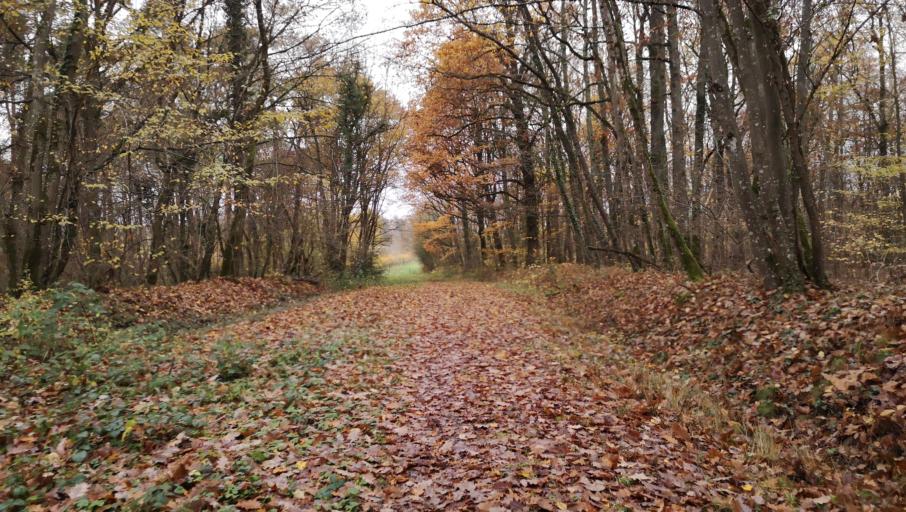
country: FR
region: Centre
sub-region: Departement du Loiret
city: Saint-Jean-de-Braye
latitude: 47.9279
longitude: 1.9825
